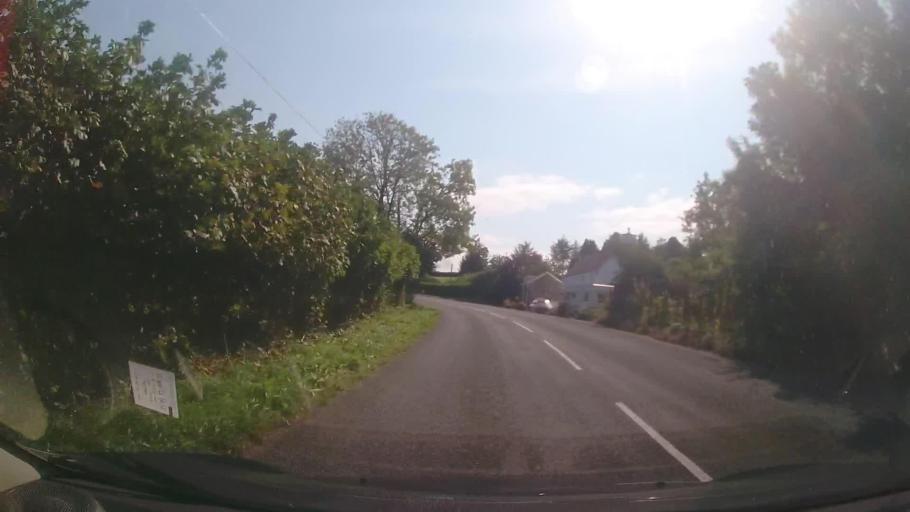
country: GB
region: Wales
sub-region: Pembrokeshire
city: Saundersfoot
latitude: 51.7438
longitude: -4.6806
